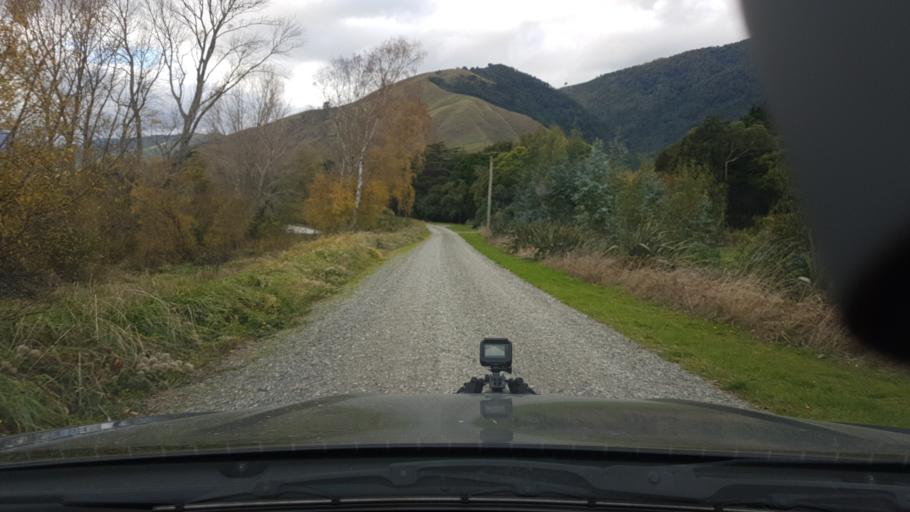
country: NZ
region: Marlborough
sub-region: Marlborough District
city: Picton
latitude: -41.3352
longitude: 173.7641
